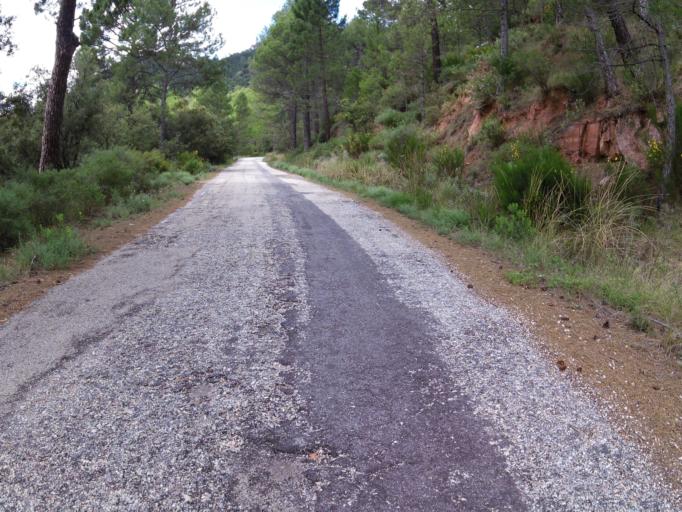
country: ES
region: Castille-La Mancha
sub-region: Provincia de Albacete
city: Paterna del Madera
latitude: 38.5801
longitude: -2.3464
